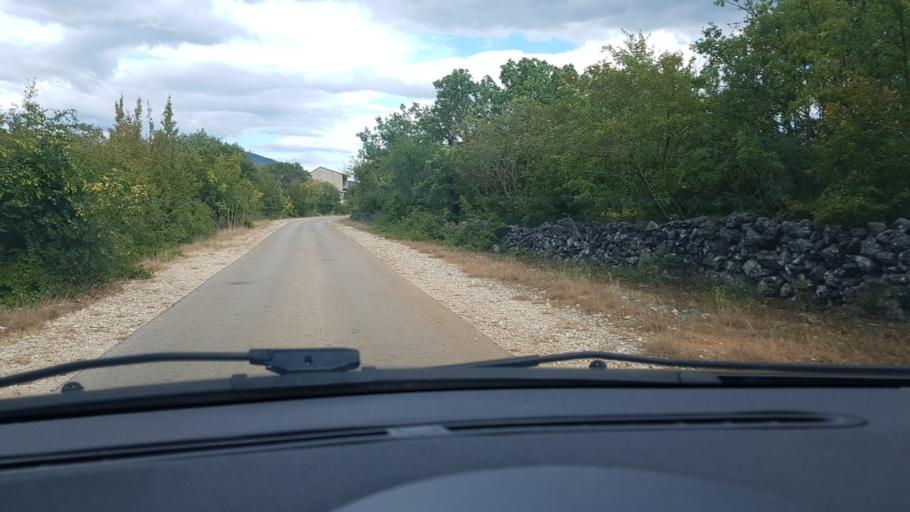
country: HR
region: Sibensko-Kniniska
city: Kistanje
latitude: 44.1107
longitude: 15.9237
